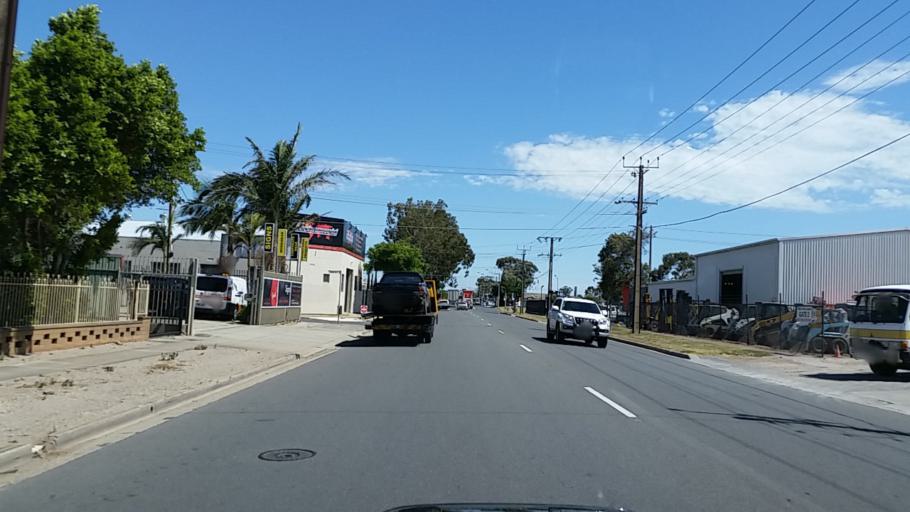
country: AU
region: South Australia
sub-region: Charles Sturt
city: Woodville North
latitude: -34.8481
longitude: 138.5466
